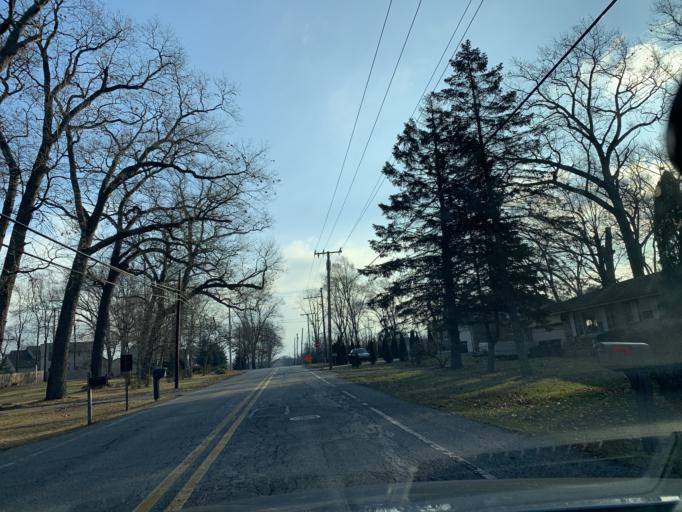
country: US
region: Indiana
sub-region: Porter County
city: Portage
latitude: 41.5867
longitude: -87.1546
